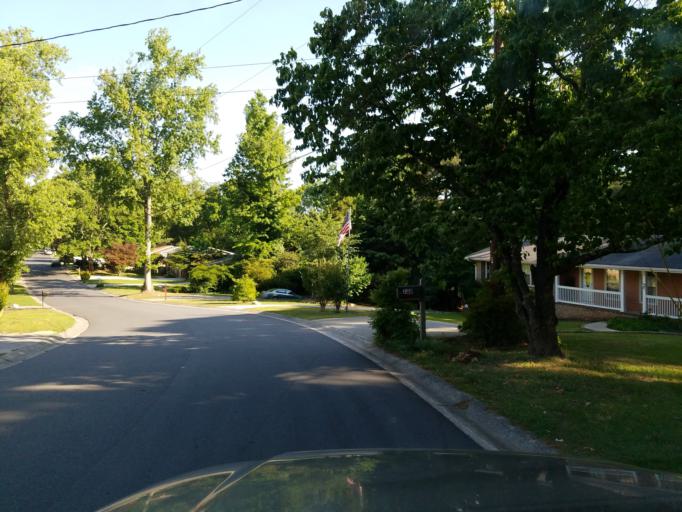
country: US
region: Georgia
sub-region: Cobb County
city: Smyrna
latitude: 33.9341
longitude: -84.4916
